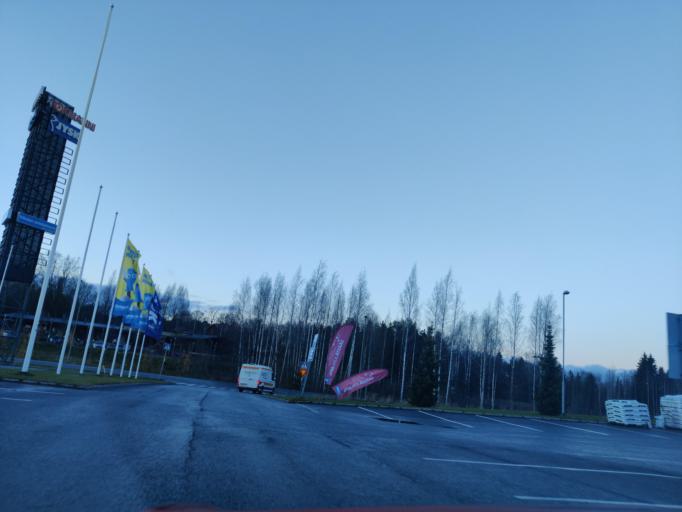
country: FI
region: Pirkanmaa
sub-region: Tampere
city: Nokia
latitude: 61.4680
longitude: 23.5114
